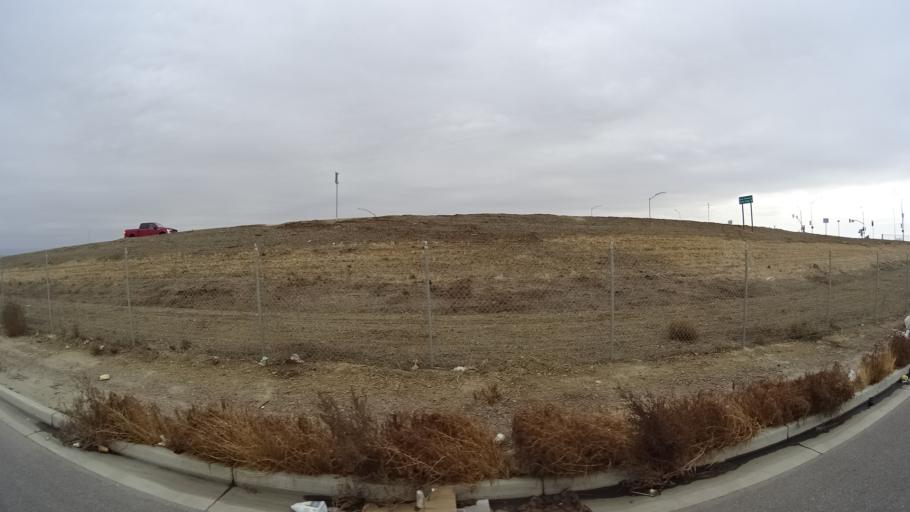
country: US
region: California
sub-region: Kern County
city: Greenfield
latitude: 35.2825
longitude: -119.0290
